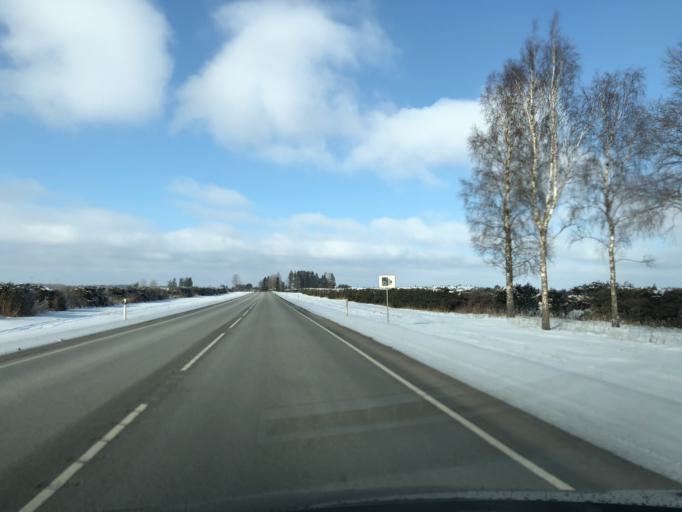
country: EE
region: Jaervamaa
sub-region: Paide linn
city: Paide
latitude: 58.8428
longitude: 25.7393
